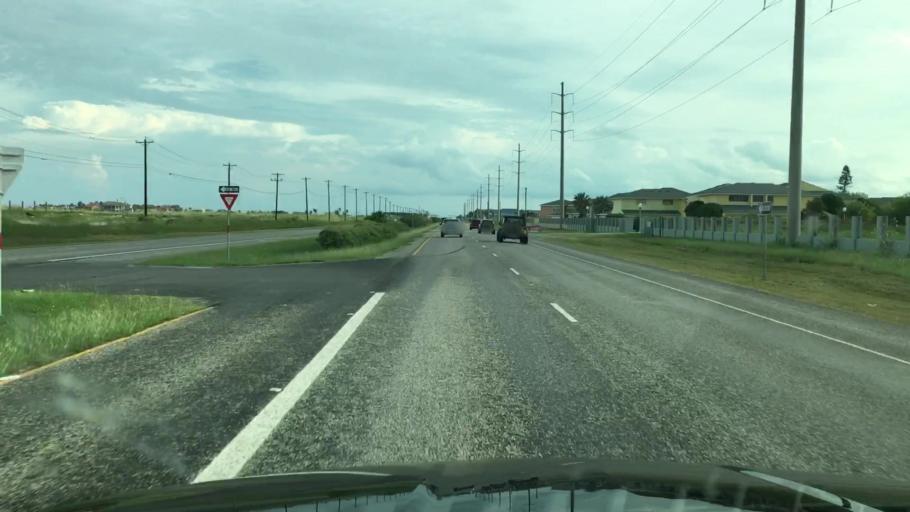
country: US
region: Texas
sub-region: Nueces County
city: Corpus Christi
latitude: 27.6138
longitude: -97.2219
